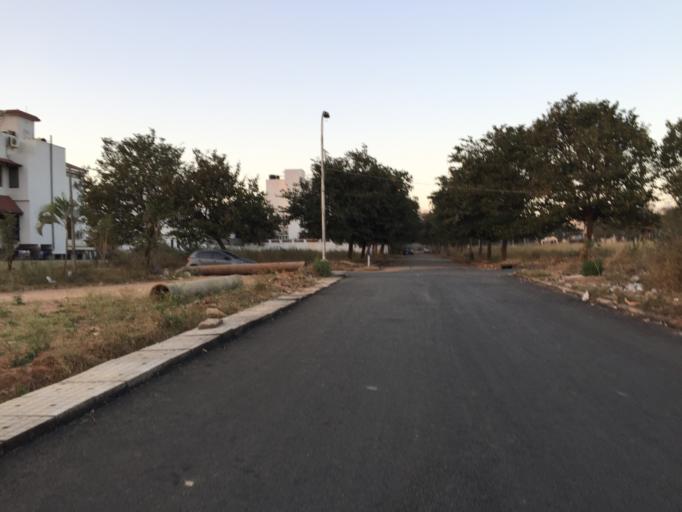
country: IN
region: Karnataka
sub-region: Bangalore Urban
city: Yelahanka
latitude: 13.0518
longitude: 77.6220
